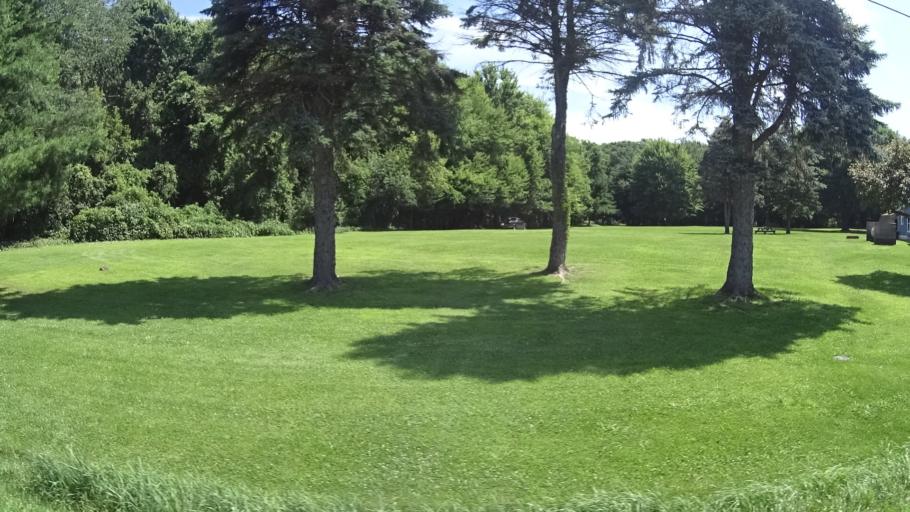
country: US
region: Ohio
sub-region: Lorain County
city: Vermilion
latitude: 41.3576
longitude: -82.4344
